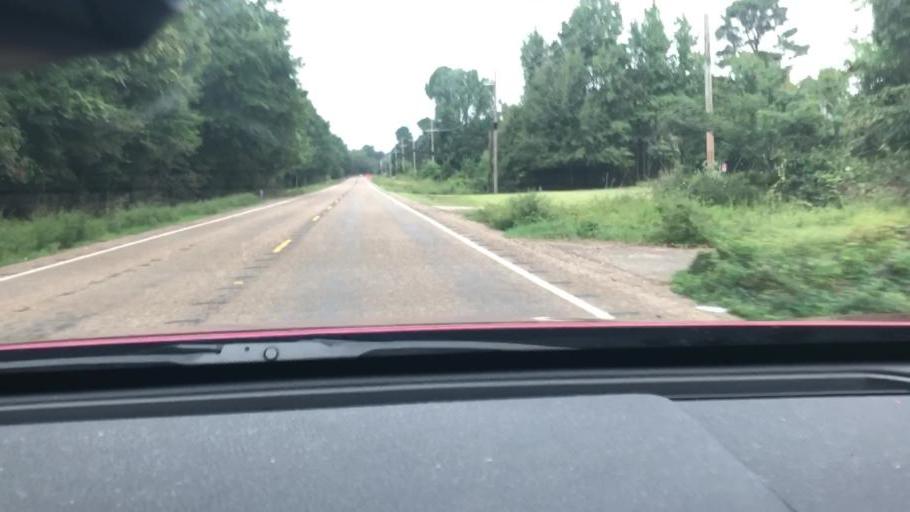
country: US
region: Texas
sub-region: Bowie County
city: Wake Village
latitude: 33.3792
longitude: -94.1026
